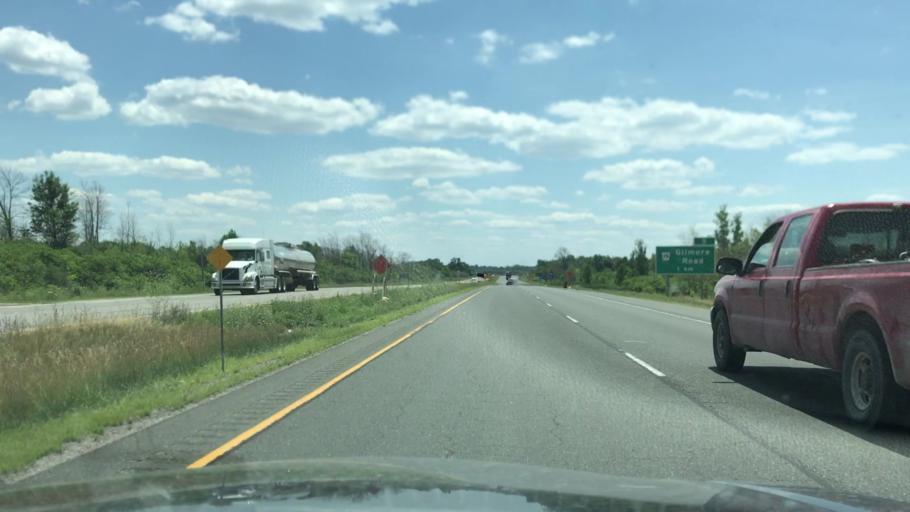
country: CA
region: Ontario
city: Fort Erie
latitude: 42.9300
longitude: -78.9797
